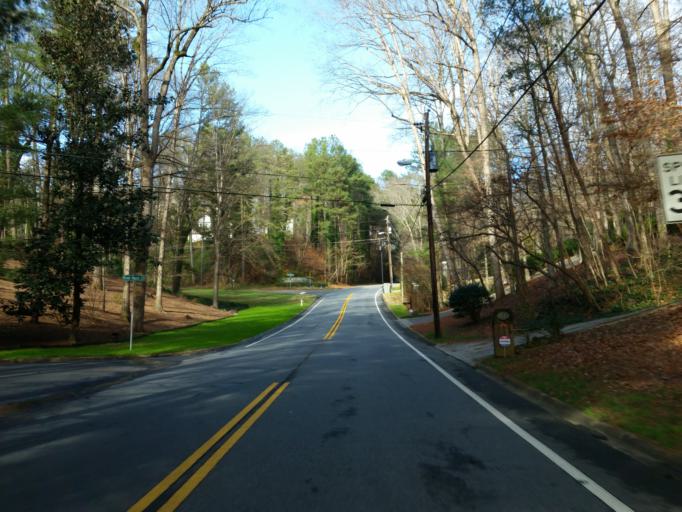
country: US
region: Georgia
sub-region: Fulton County
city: Sandy Springs
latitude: 33.9480
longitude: -84.3939
